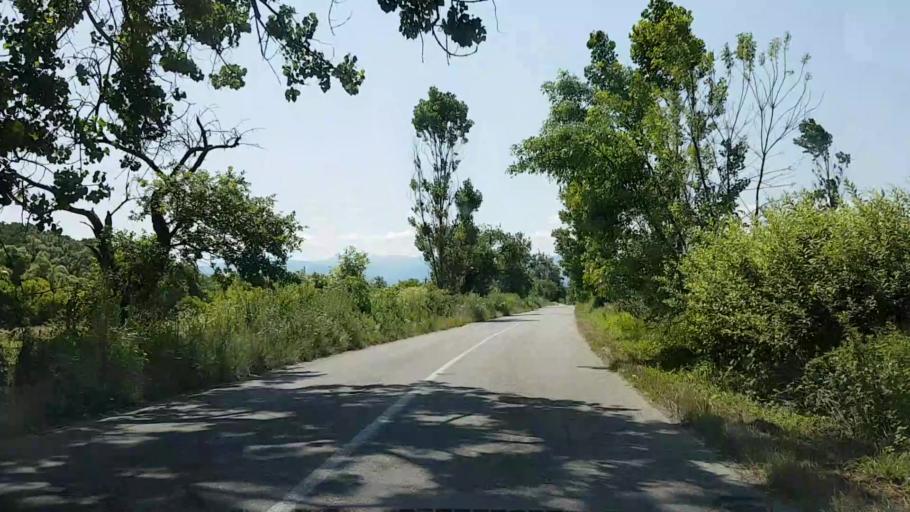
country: RO
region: Brasov
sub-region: Comuna Voila
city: Voila
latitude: 45.8522
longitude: 24.8319
